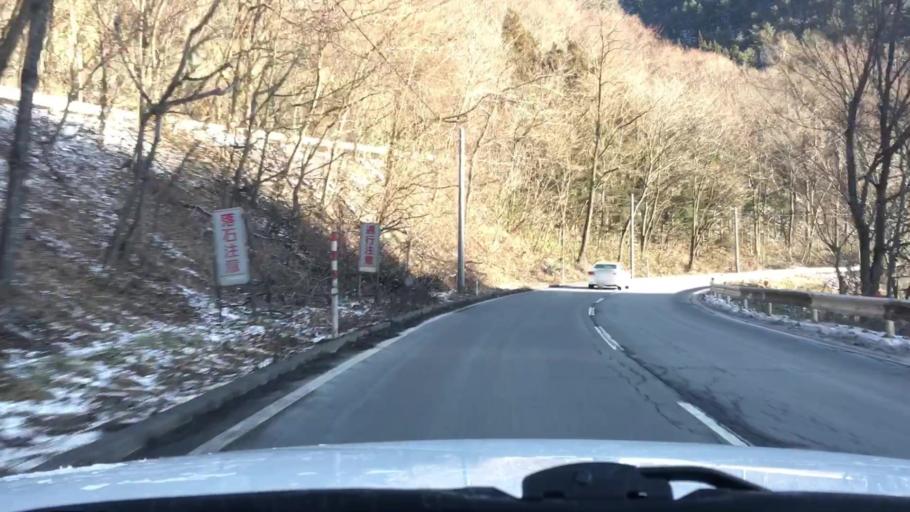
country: JP
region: Iwate
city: Morioka-shi
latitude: 39.6672
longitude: 141.3170
